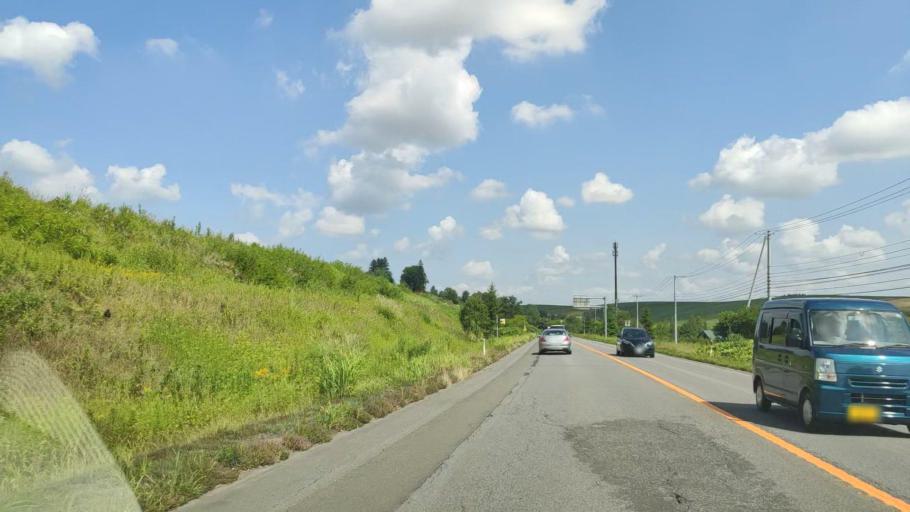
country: JP
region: Hokkaido
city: Shimo-furano
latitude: 43.5476
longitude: 142.4392
